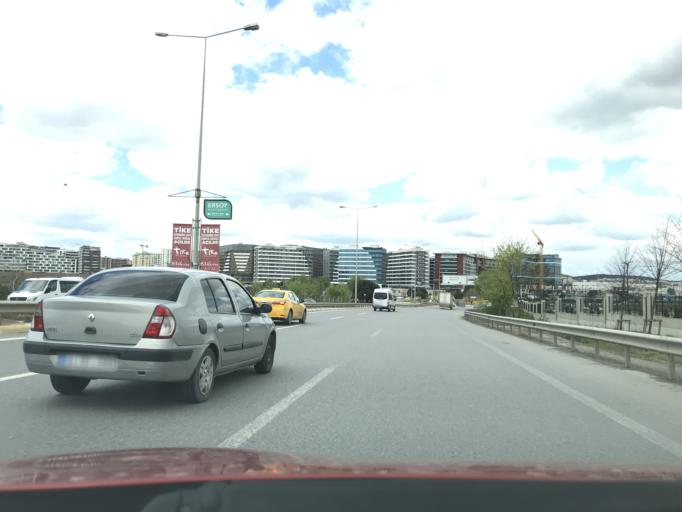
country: TR
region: Istanbul
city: Sultanbeyli
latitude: 40.9219
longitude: 29.3128
